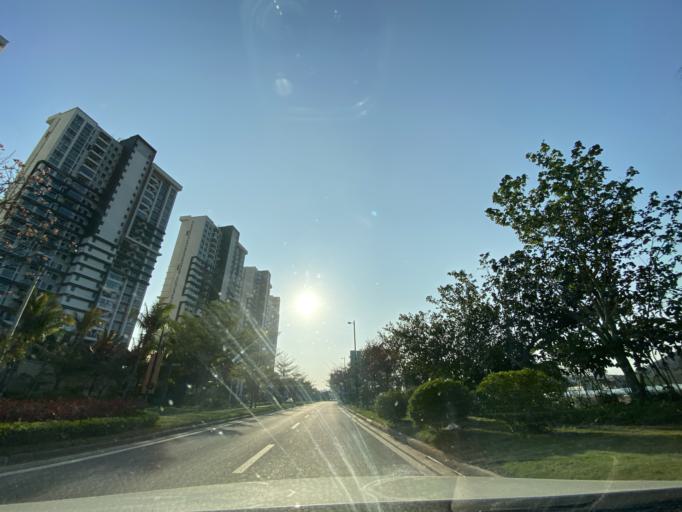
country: CN
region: Hainan
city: Xincun
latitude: 18.4212
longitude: 109.9203
